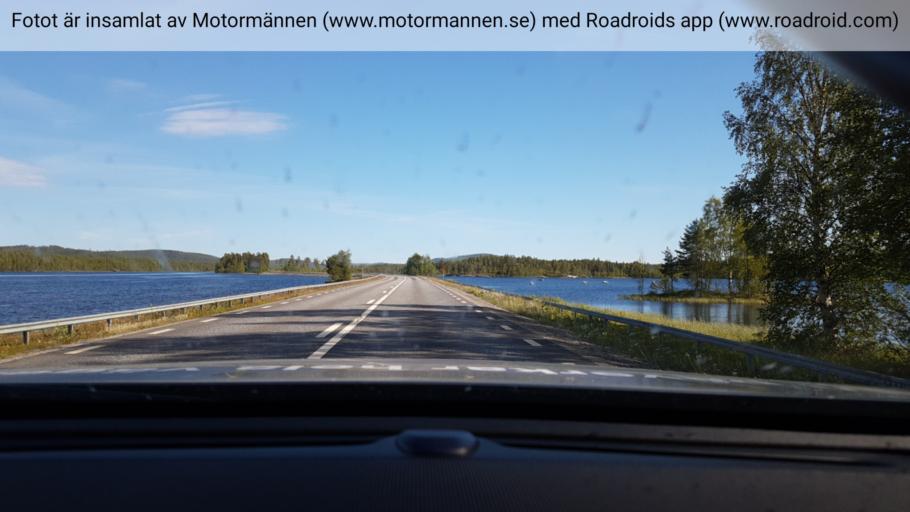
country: SE
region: Vaesterbotten
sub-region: Lycksele Kommun
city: Soderfors
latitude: 64.7566
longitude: 18.1698
